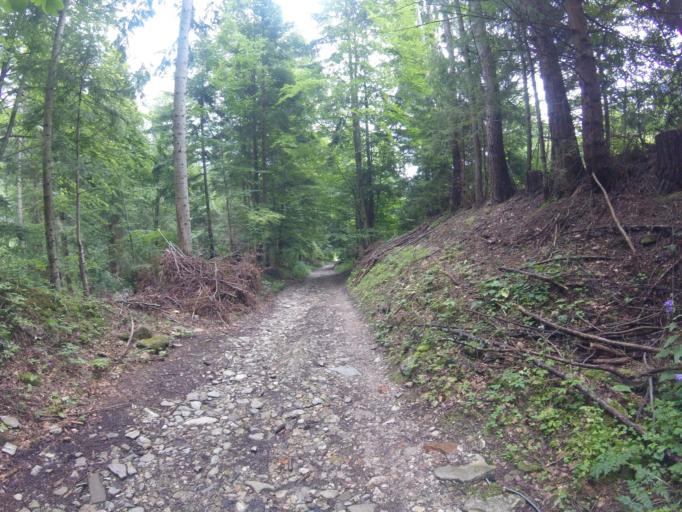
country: SK
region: Zilinsky
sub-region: Okres Zilina
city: Terchova
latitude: 49.2304
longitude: 19.0245
